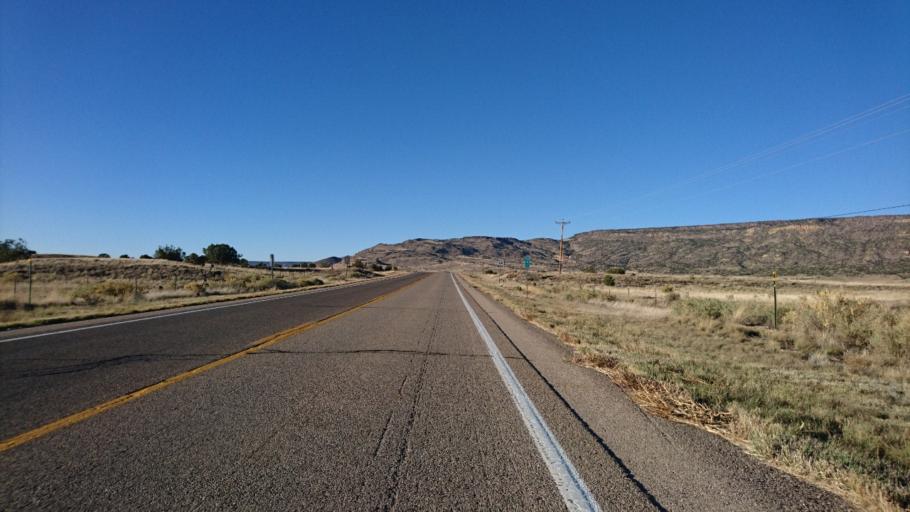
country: US
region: New Mexico
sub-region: Cibola County
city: Grants
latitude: 35.0898
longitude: -107.7704
